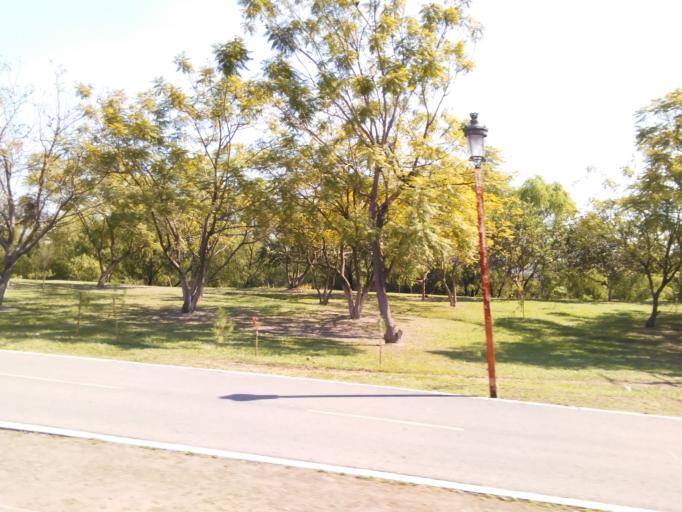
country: MX
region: Nayarit
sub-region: Tepic
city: La Corregidora
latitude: 21.4790
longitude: -104.8513
